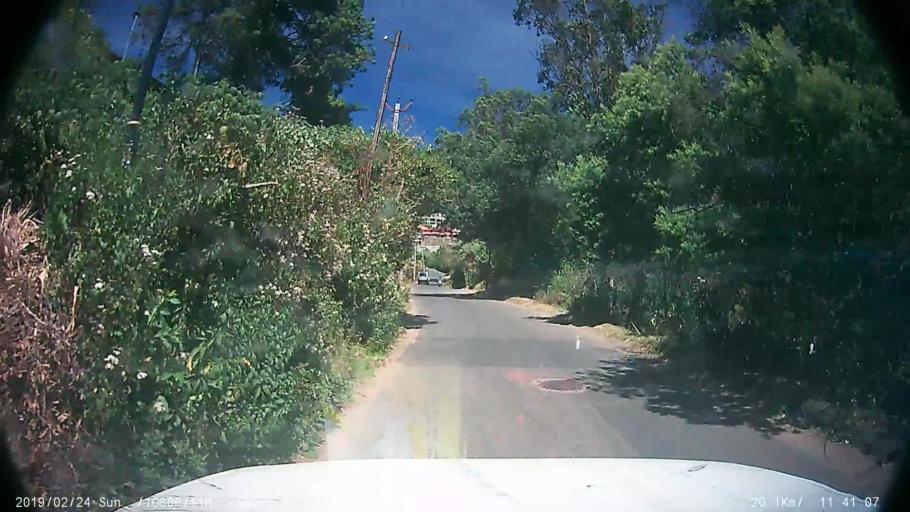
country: IN
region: Tamil Nadu
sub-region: Nilgiri
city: Ooty
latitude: 11.4166
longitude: 76.7051
